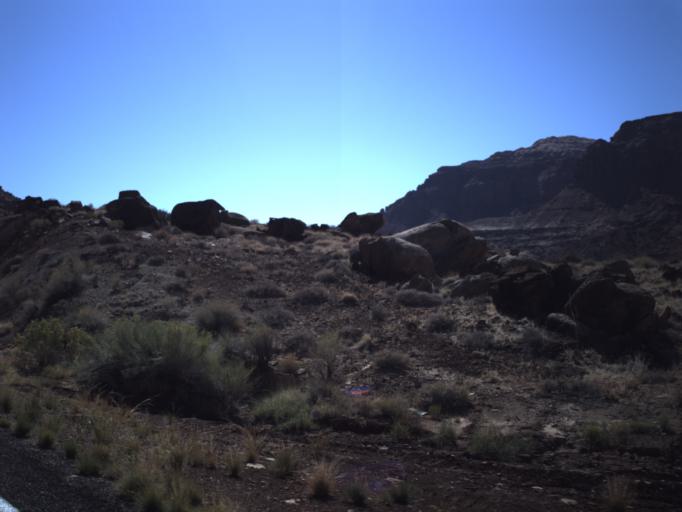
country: US
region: Utah
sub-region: San Juan County
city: Blanding
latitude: 37.8930
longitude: -110.4368
